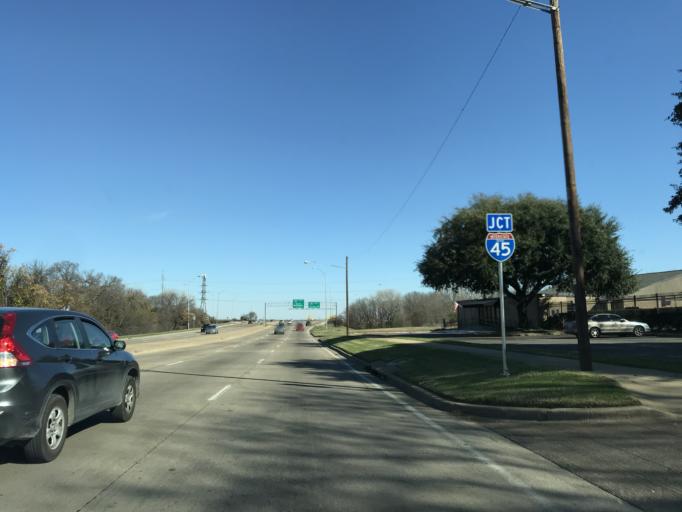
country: US
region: Texas
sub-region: Dallas County
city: Hutchins
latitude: 32.6986
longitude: -96.7592
